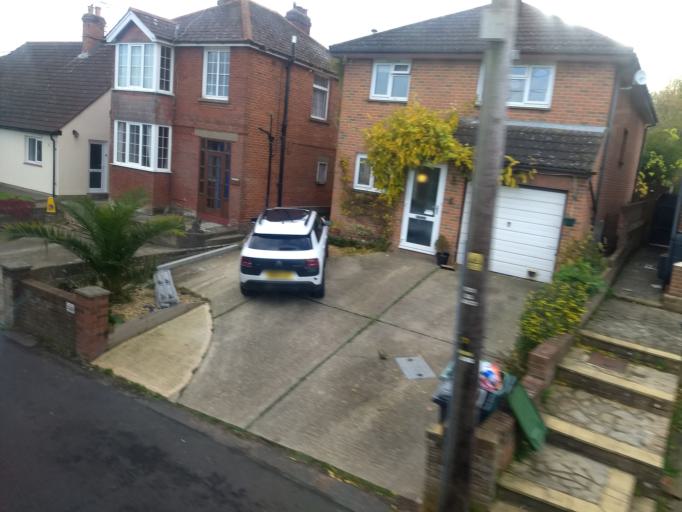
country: GB
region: England
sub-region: Isle of Wight
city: Newport
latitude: 50.6945
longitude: -1.3201
